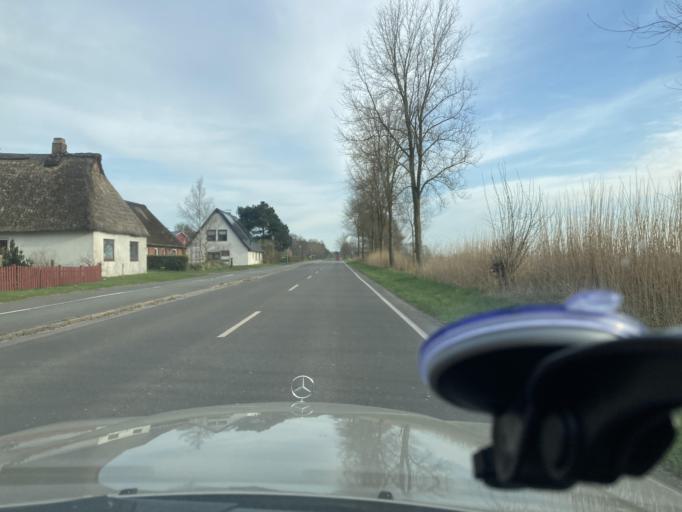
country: DE
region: Schleswig-Holstein
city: Krempel
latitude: 54.2971
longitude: 9.0392
